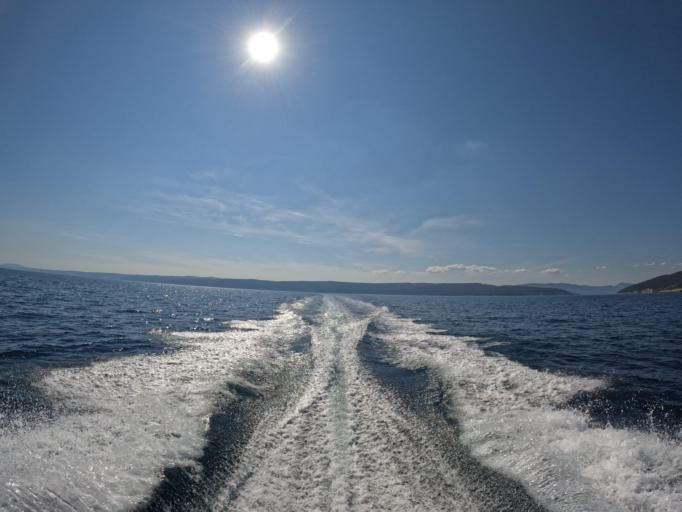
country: HR
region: Primorsko-Goranska
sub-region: Grad Krk
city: Krk
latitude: 44.9487
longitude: 14.5352
